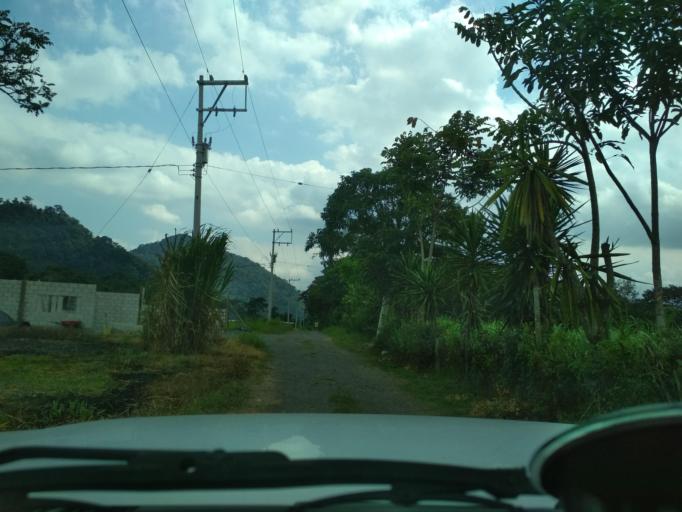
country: MX
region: Veracruz
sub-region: Ixtaczoquitlan
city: Buenavista
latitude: 18.9008
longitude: -97.0271
